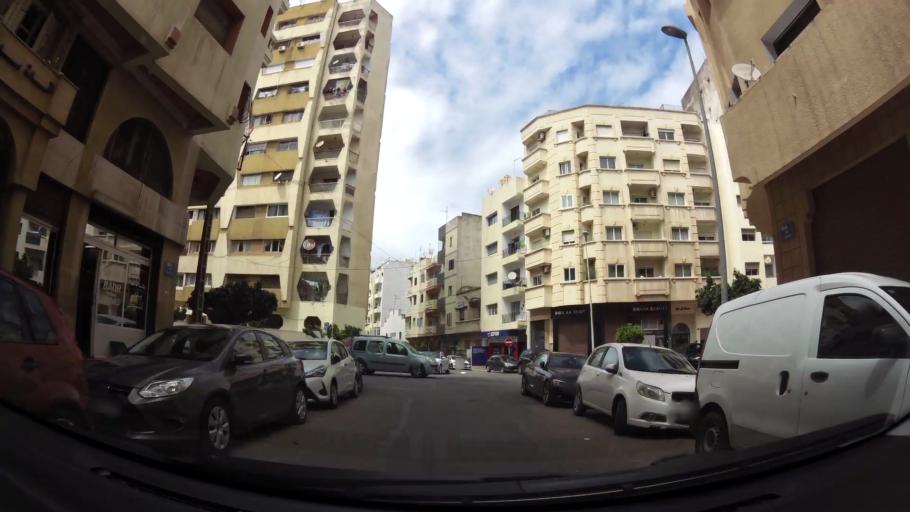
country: MA
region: Grand Casablanca
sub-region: Casablanca
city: Casablanca
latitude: 33.5959
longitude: -7.6404
